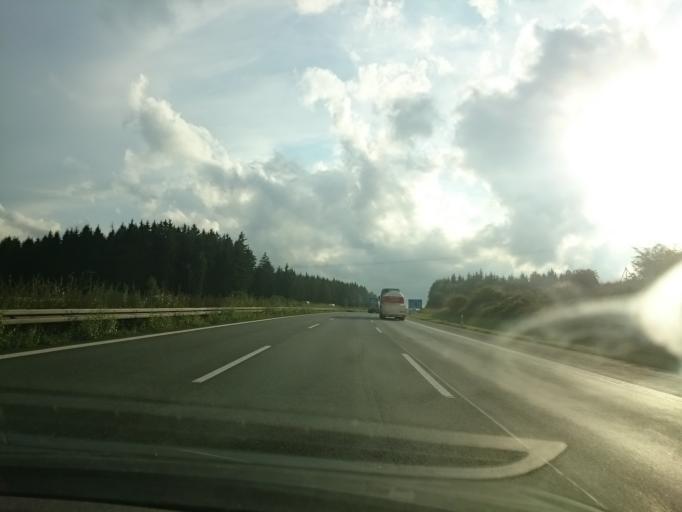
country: DE
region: Bavaria
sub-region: Upper Franconia
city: Marktschorgast
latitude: 50.0918
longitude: 11.6886
